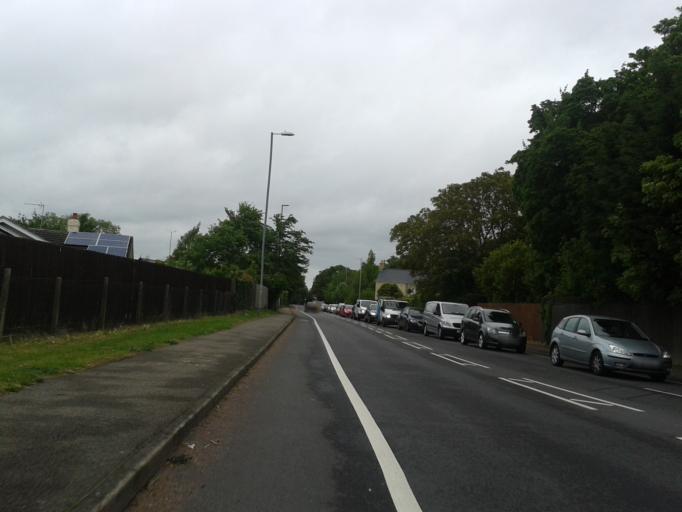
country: GB
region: England
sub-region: Cambridgeshire
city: Histon
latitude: 52.2454
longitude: 0.1106
